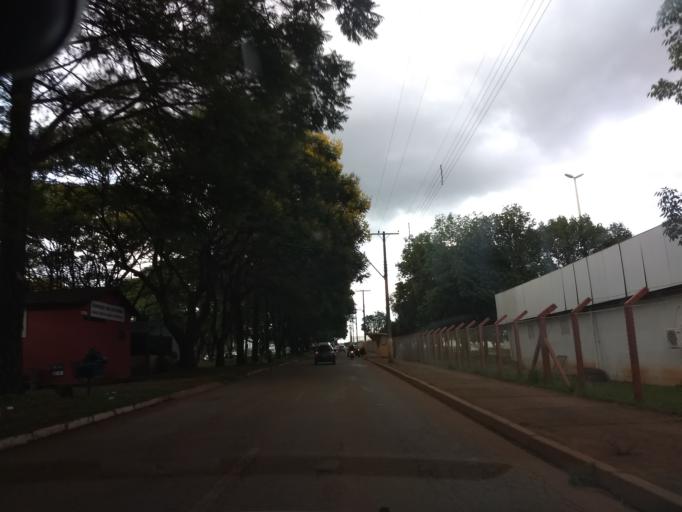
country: BR
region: Federal District
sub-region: Brasilia
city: Brasilia
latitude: -15.8112
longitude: -47.9579
